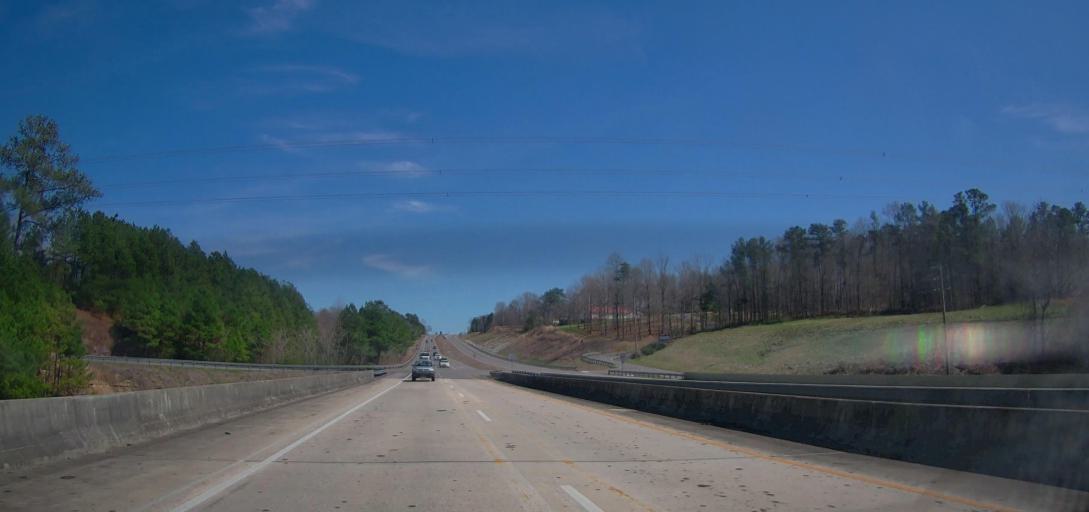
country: US
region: Alabama
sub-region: Cullman County
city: Cullman
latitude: 34.1828
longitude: -86.7737
